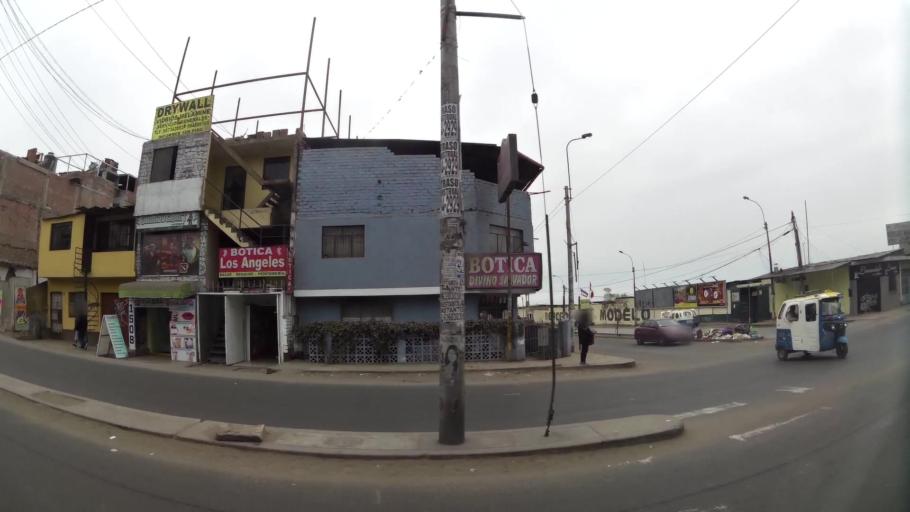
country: PE
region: Lima
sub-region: Lima
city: Surco
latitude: -12.2091
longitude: -76.9466
